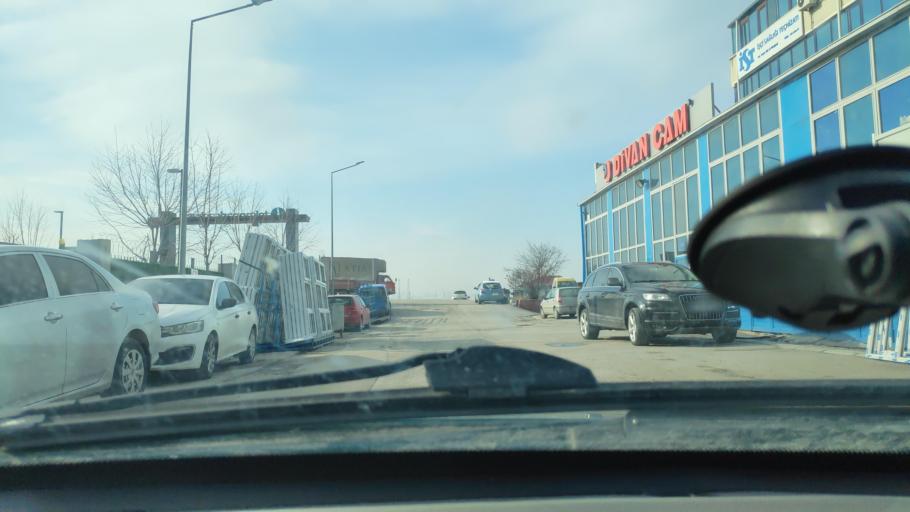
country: TR
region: Ankara
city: Batikent
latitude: 39.9955
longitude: 32.7504
